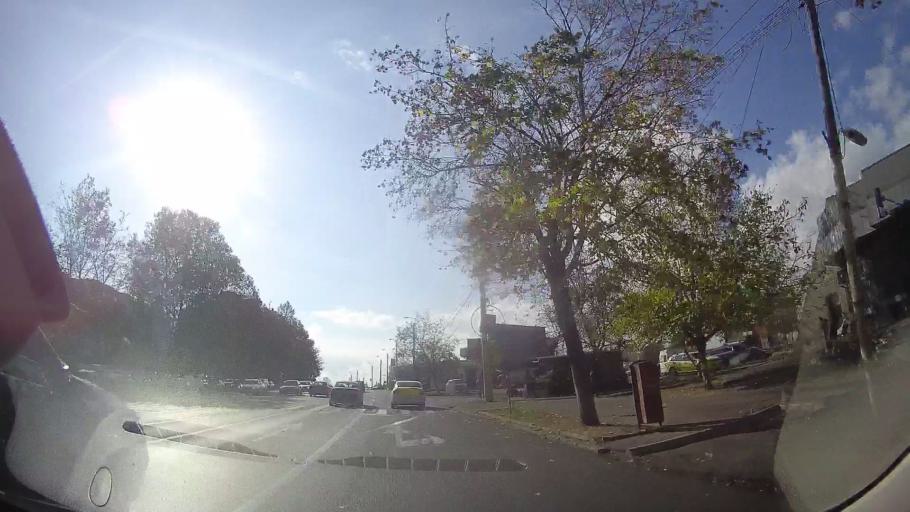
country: RO
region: Constanta
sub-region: Municipiul Constanta
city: Constanta
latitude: 44.1548
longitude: 28.6291
